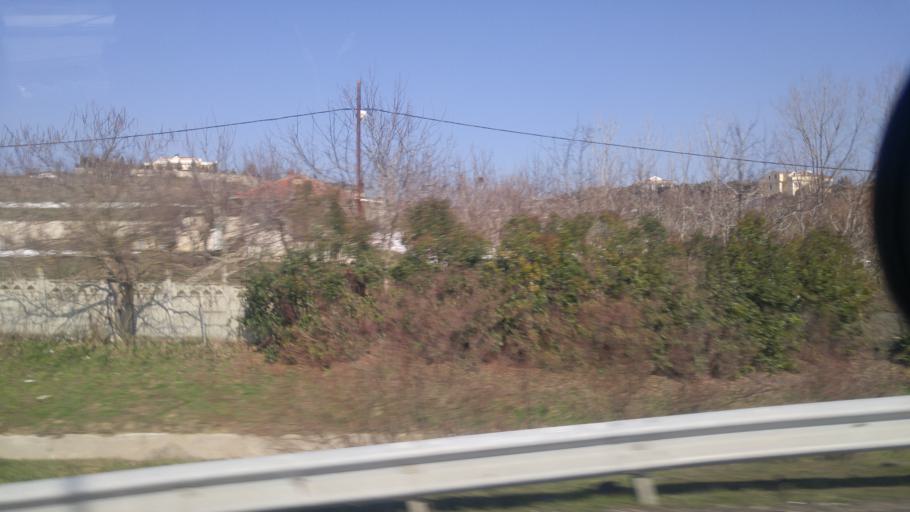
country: TR
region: Istanbul
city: Celaliye
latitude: 41.0589
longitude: 28.4135
